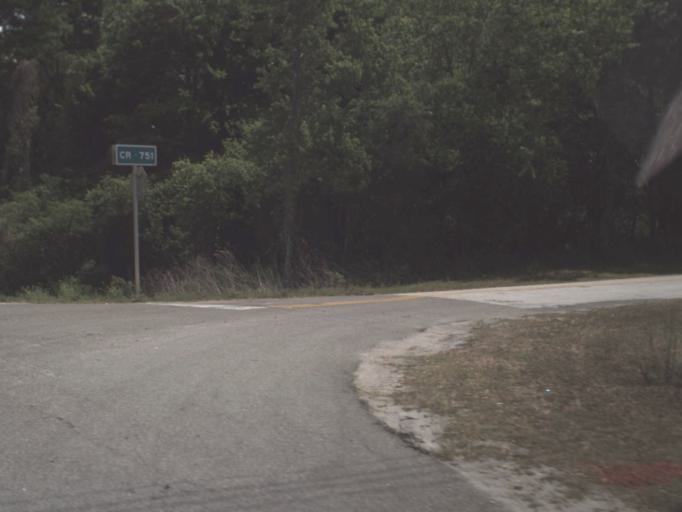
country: US
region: Florida
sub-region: Hernando County
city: Ridge Manor
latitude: 28.5552
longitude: -82.0754
